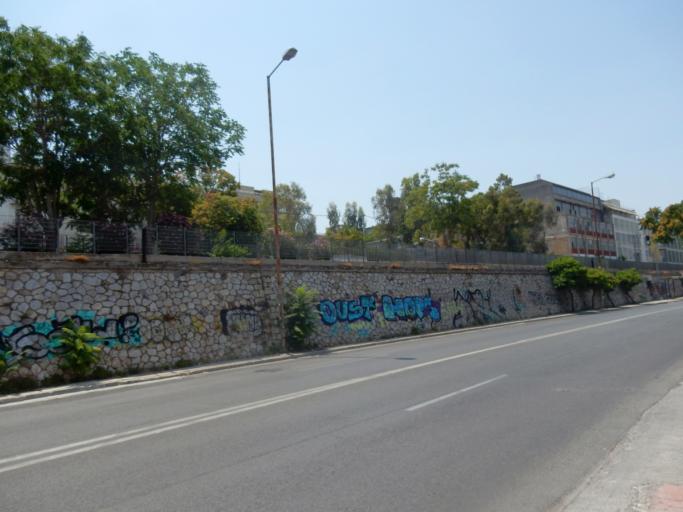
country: GR
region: Attica
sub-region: Nomarchia Athinas
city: Nea Ionia
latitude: 38.0355
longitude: 23.7479
